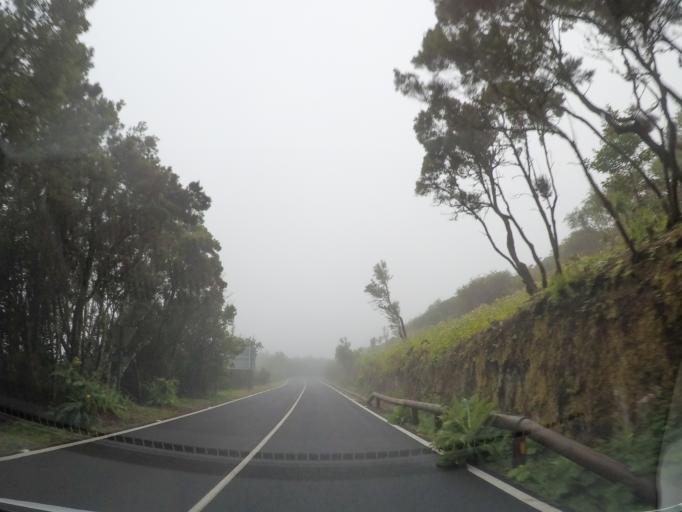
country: ES
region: Canary Islands
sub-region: Provincia de Santa Cruz de Tenerife
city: Alajero
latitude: 28.1075
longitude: -17.2427
